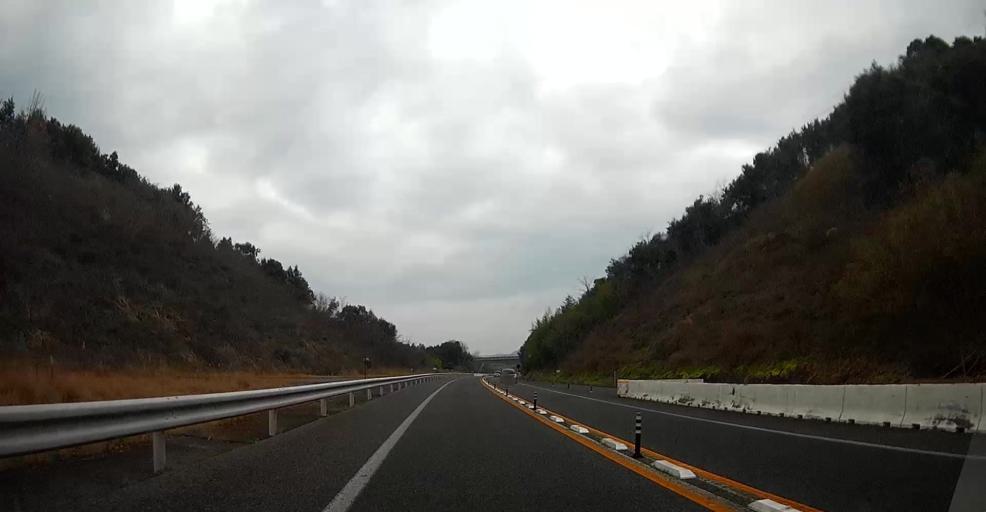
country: JP
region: Kumamoto
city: Hondo
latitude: 32.5117
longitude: 130.3603
